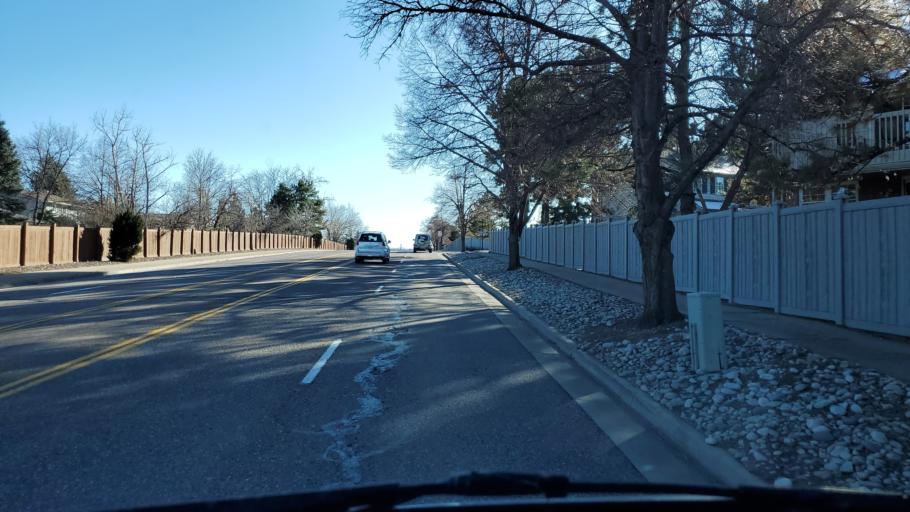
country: US
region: Colorado
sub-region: Arapahoe County
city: Castlewood
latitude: 39.5867
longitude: -104.9043
